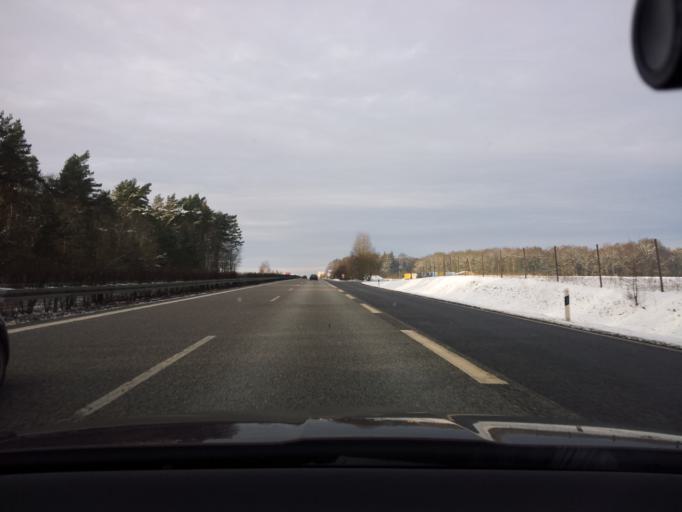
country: DE
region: Mecklenburg-Vorpommern
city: Wittenburg
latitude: 53.4949
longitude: 11.1330
